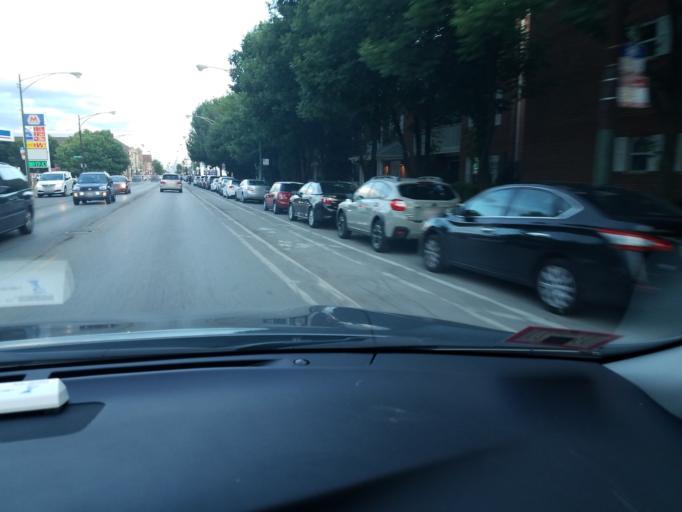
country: US
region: Illinois
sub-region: Cook County
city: Lincolnwood
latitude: 41.9671
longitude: -87.7387
